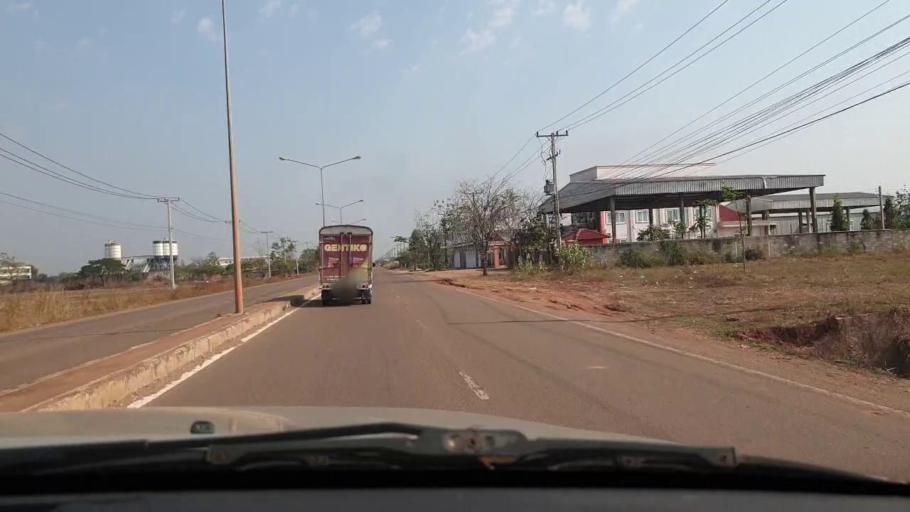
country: LA
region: Vientiane
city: Vientiane
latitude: 18.0118
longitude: 102.7224
